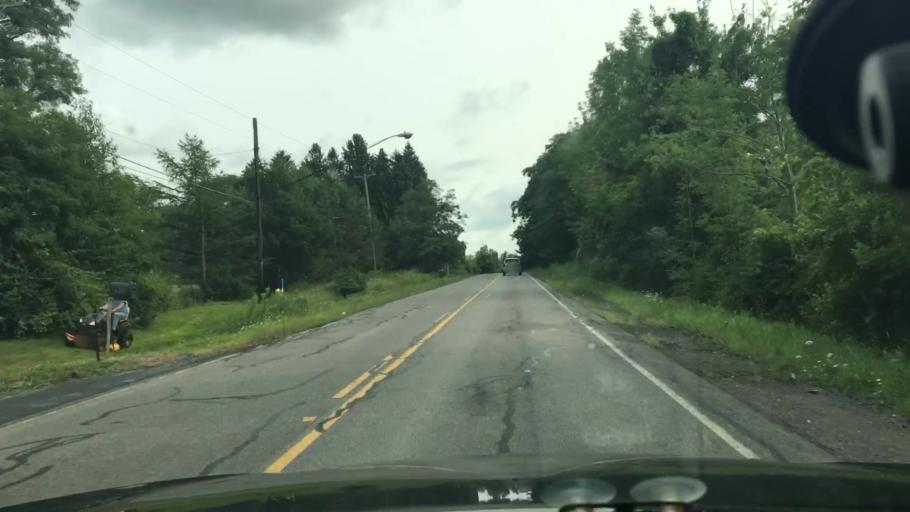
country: US
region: New York
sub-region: Erie County
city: Orchard Park
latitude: 42.7239
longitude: -78.7330
